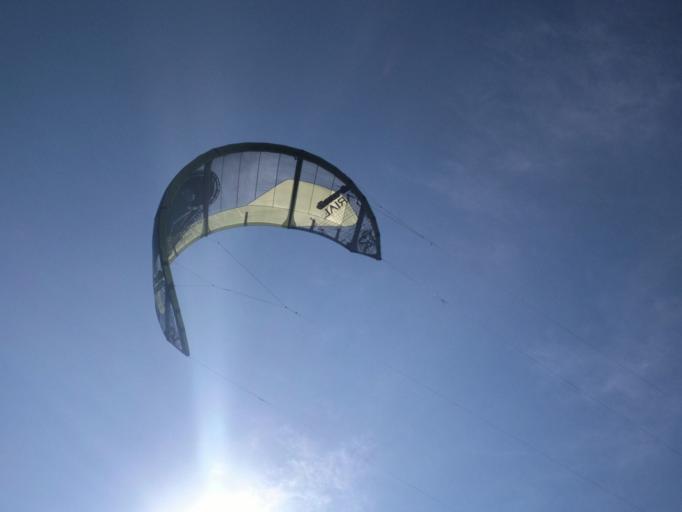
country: NL
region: North Holland
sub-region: Gemeente Texel
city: Den Burg
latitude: 53.0845
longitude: 4.7374
